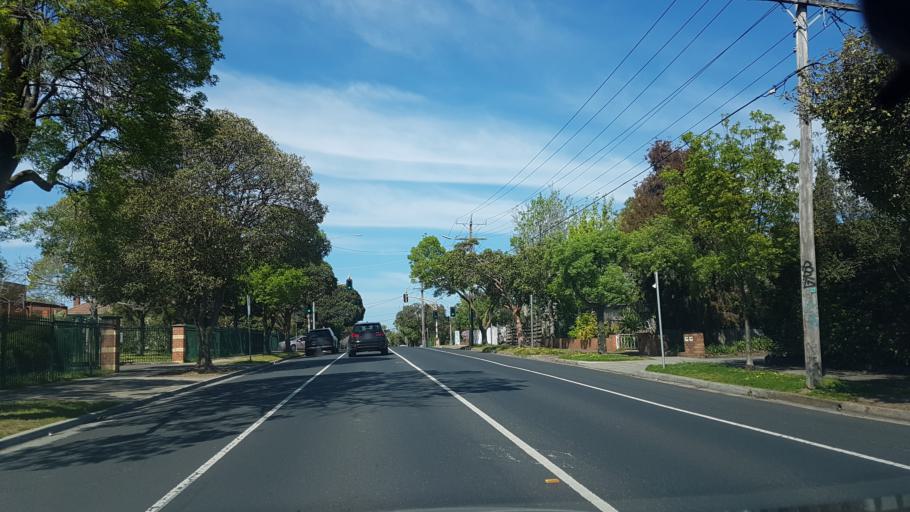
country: AU
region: Victoria
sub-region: Bayside
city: Moorabbin
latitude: -37.9321
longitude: 145.0488
